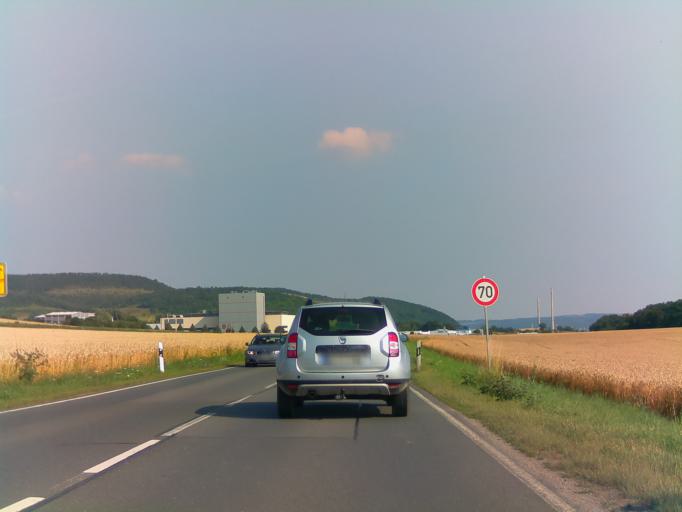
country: DE
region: Thuringia
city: Rothenstein
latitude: 50.8545
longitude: 11.6026
